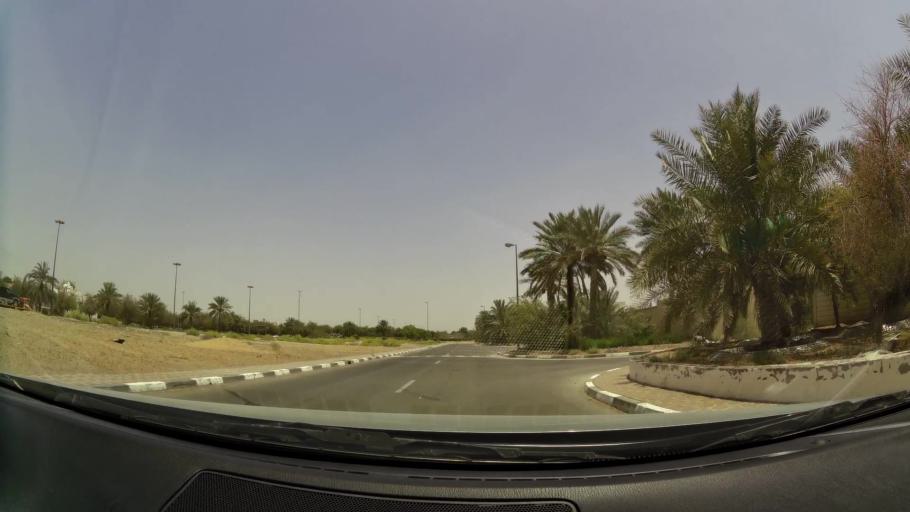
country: OM
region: Al Buraimi
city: Al Buraymi
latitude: 24.2610
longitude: 55.7197
